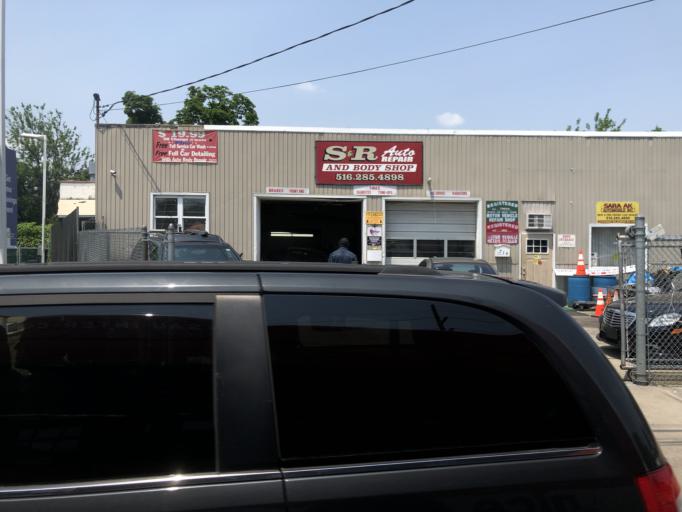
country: US
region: New York
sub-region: Nassau County
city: Elmont
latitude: 40.6925
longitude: -73.7192
